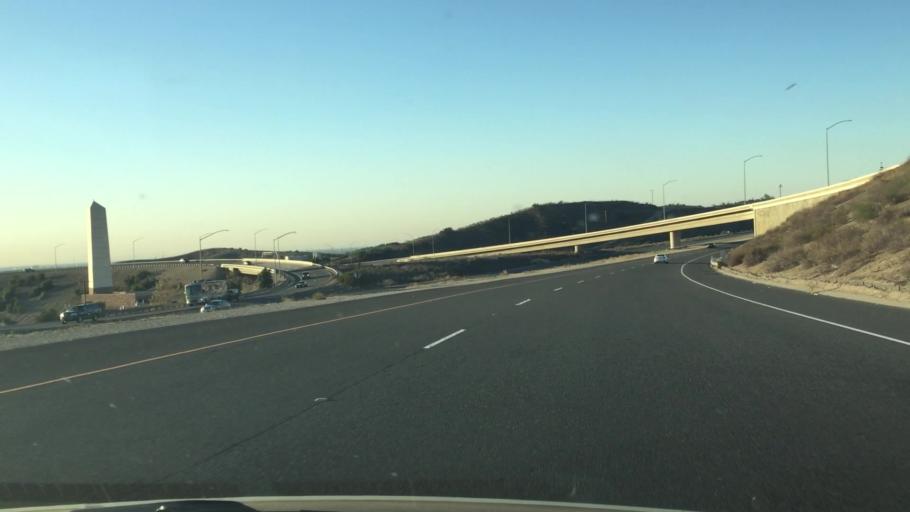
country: US
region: California
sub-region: Orange County
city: Foothill Ranch
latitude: 33.7090
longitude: -117.7182
